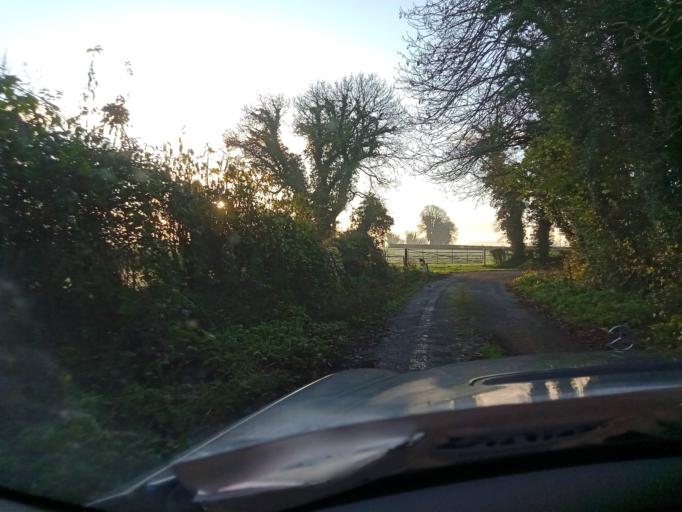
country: IE
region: Leinster
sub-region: Kilkenny
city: Callan
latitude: 52.5298
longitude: -7.4474
